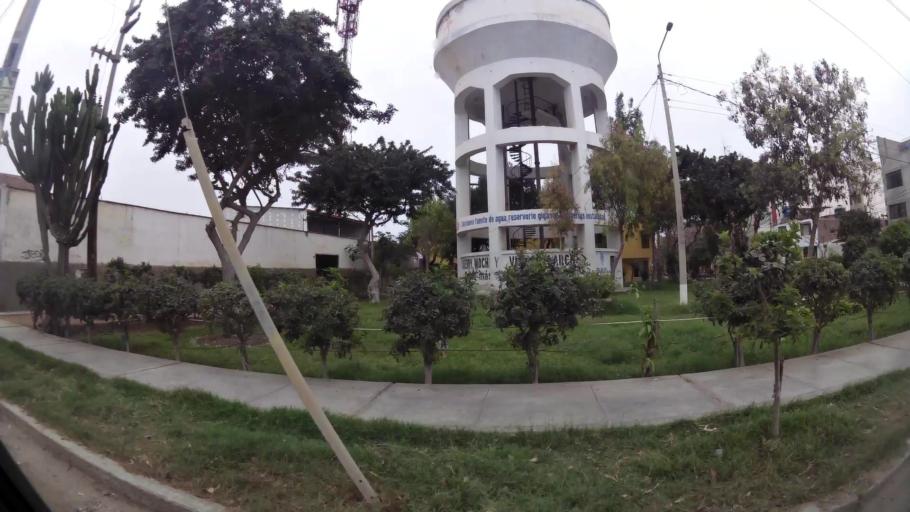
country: PE
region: La Libertad
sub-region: Provincia de Trujillo
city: Buenos Aires
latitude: -8.1361
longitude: -79.0417
